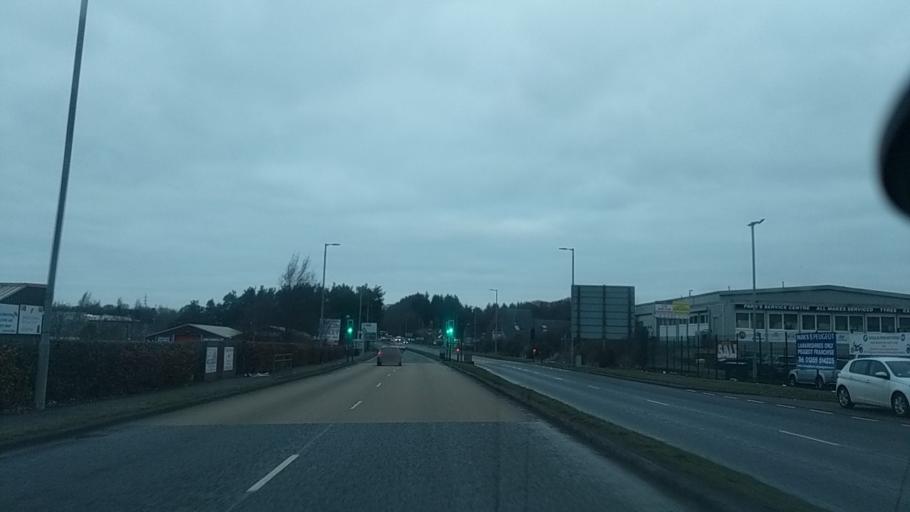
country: GB
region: Scotland
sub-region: South Lanarkshire
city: East Kilbride
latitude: 55.7770
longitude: -4.1634
